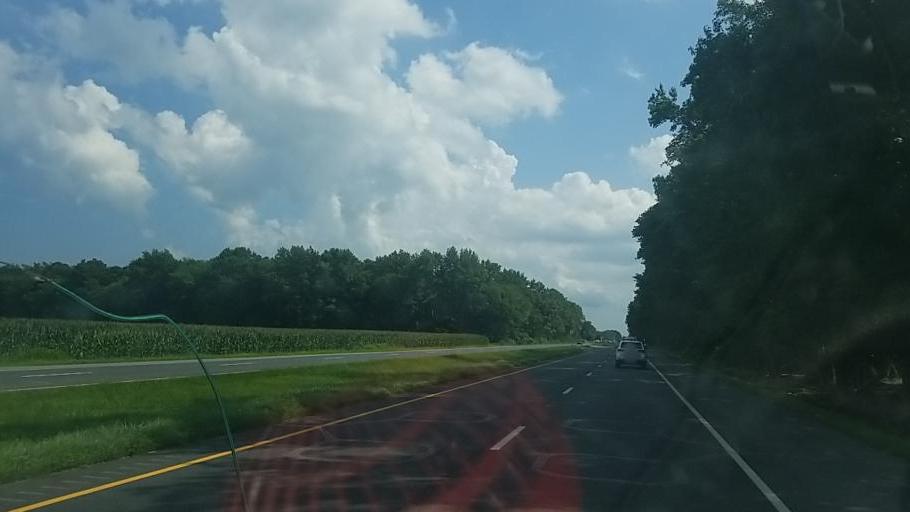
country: US
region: Delaware
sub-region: Sussex County
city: Selbyville
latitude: 38.4884
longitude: -75.2363
